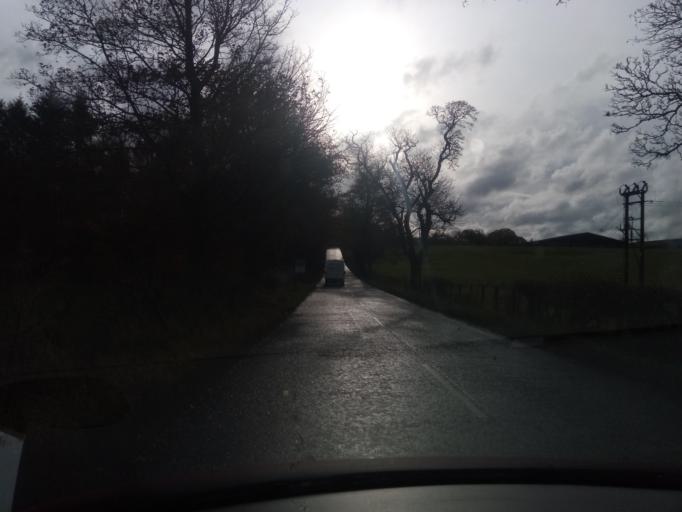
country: GB
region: England
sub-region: Northumberland
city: Birtley
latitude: 55.0648
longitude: -2.1921
